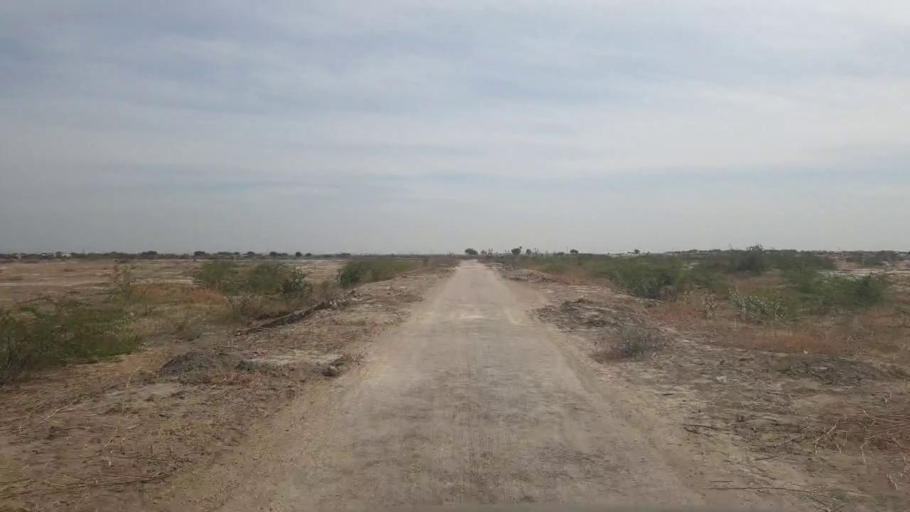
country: PK
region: Sindh
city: Kunri
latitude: 25.2155
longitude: 69.6230
